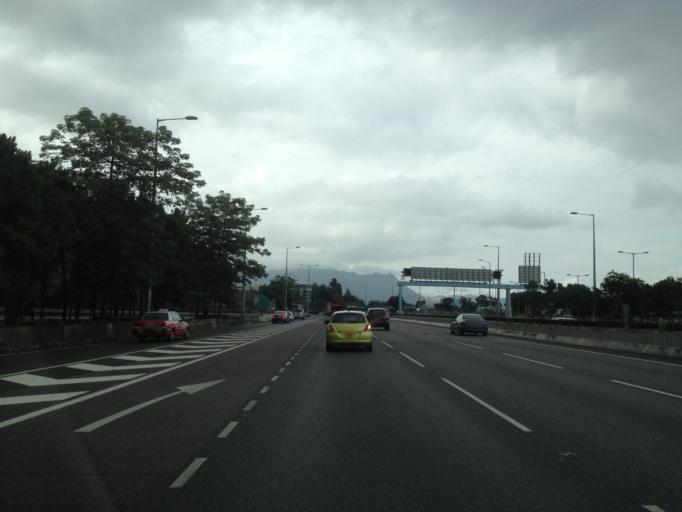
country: HK
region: Sha Tin
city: Sha Tin
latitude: 22.4159
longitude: 114.2131
